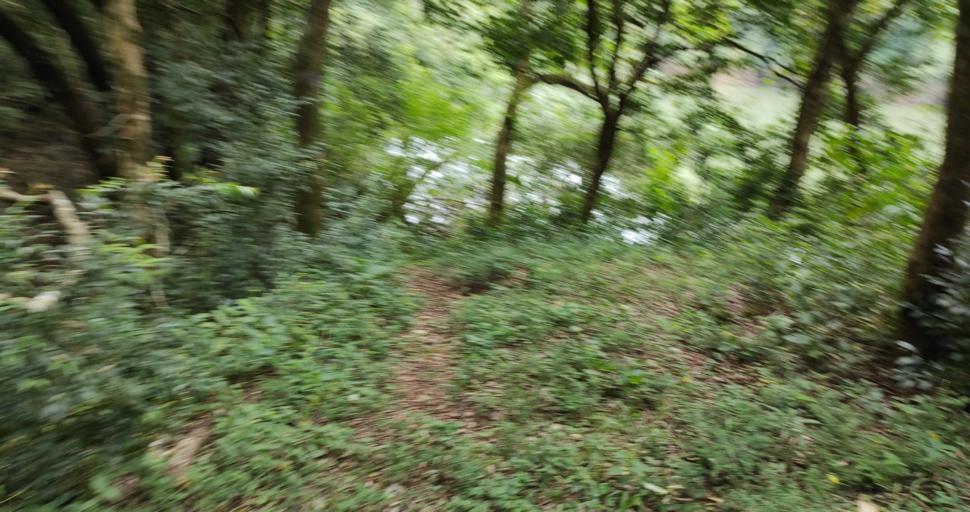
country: AR
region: Misiones
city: El Soberbio
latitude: -27.2760
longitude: -54.2204
